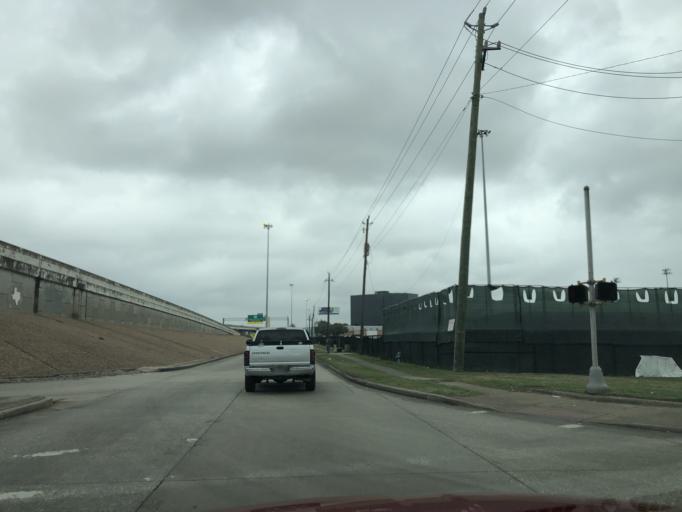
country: US
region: Texas
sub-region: Harris County
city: Aldine
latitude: 29.9152
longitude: -95.4122
